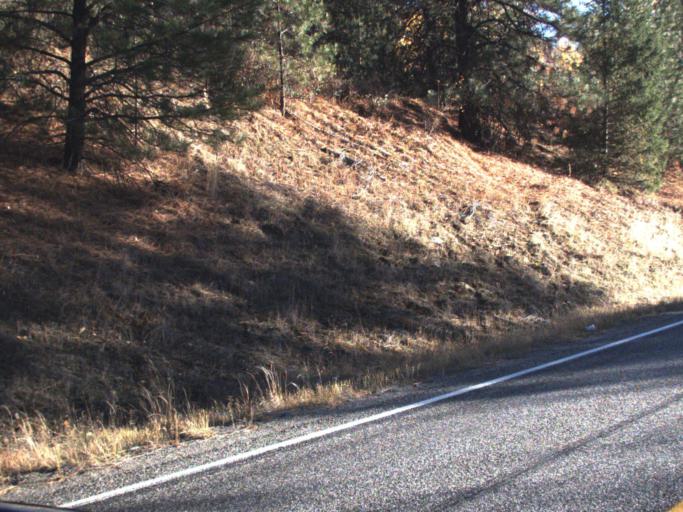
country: CA
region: British Columbia
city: Rossland
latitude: 48.9030
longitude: -117.7940
